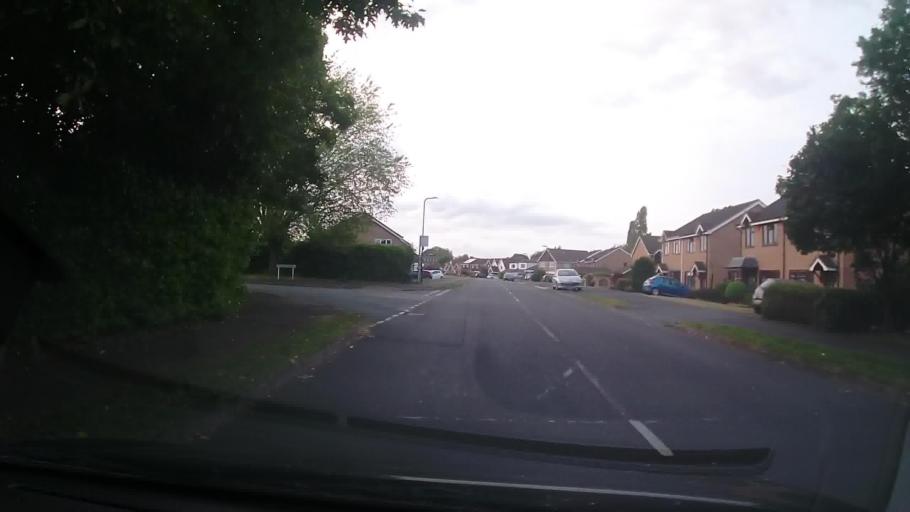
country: GB
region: England
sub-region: Shropshire
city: Shrewsbury
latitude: 52.6972
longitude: -2.7408
